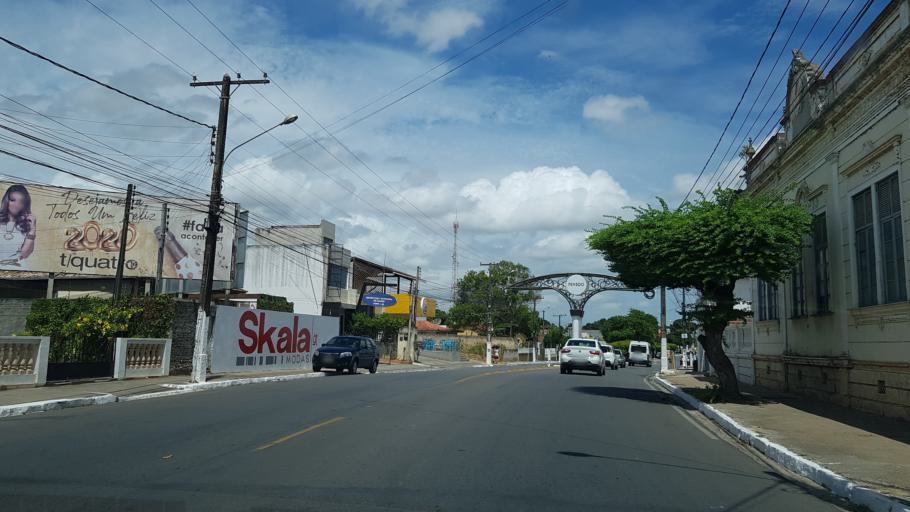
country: BR
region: Alagoas
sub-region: Penedo
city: Penedo
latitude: -10.2838
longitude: -36.5720
